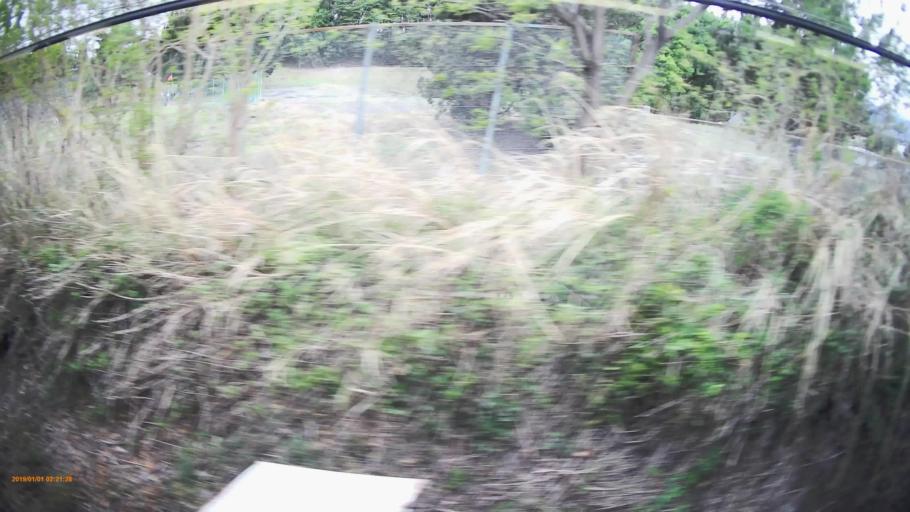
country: JP
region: Yamanashi
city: Ryuo
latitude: 35.6787
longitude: 138.4994
